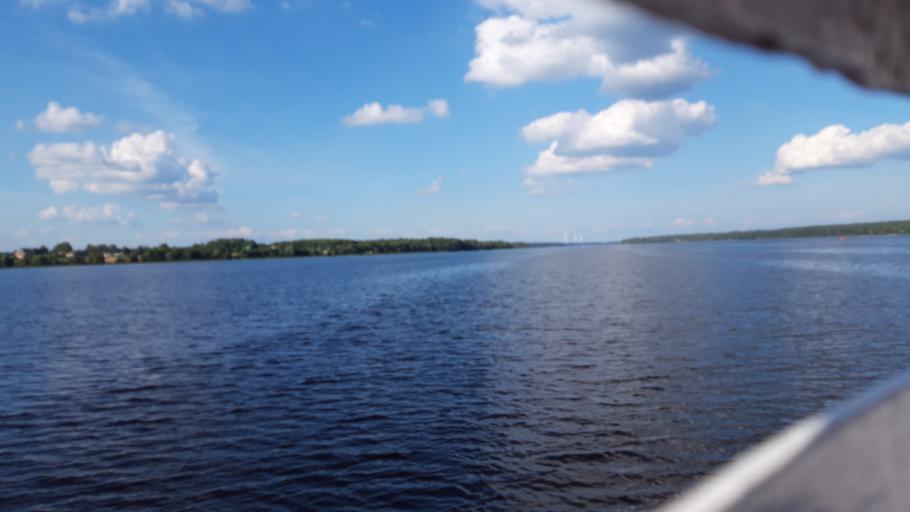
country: RU
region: Tverskaya
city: Konakovo
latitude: 56.6657
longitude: 36.6558
